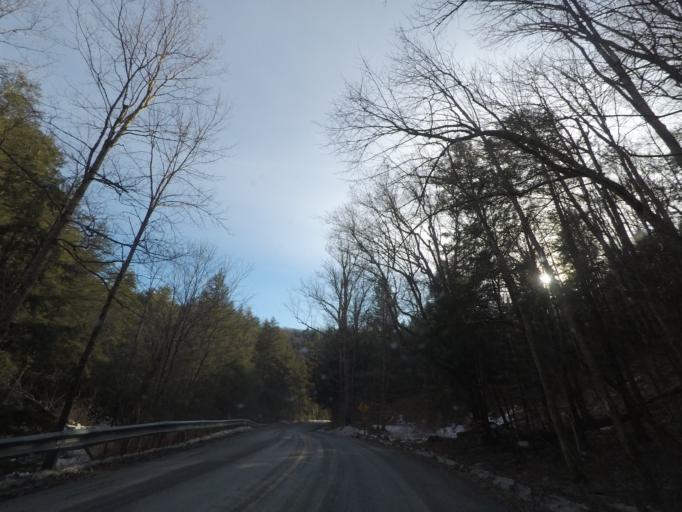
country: US
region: New York
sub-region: Rensselaer County
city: Hoosick Falls
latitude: 42.7651
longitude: -73.3546
